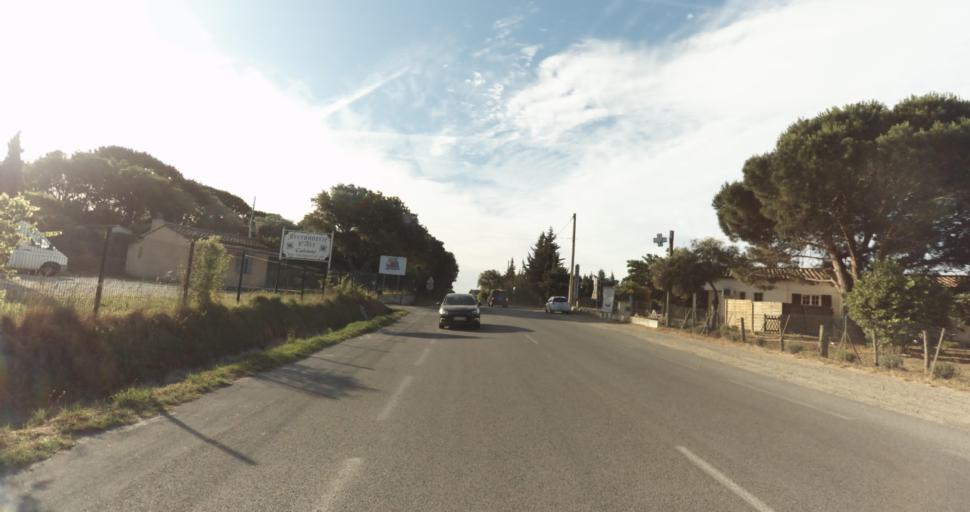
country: FR
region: Provence-Alpes-Cote d'Azur
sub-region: Departement du Var
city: Saint-Tropez
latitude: 43.2547
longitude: 6.6379
